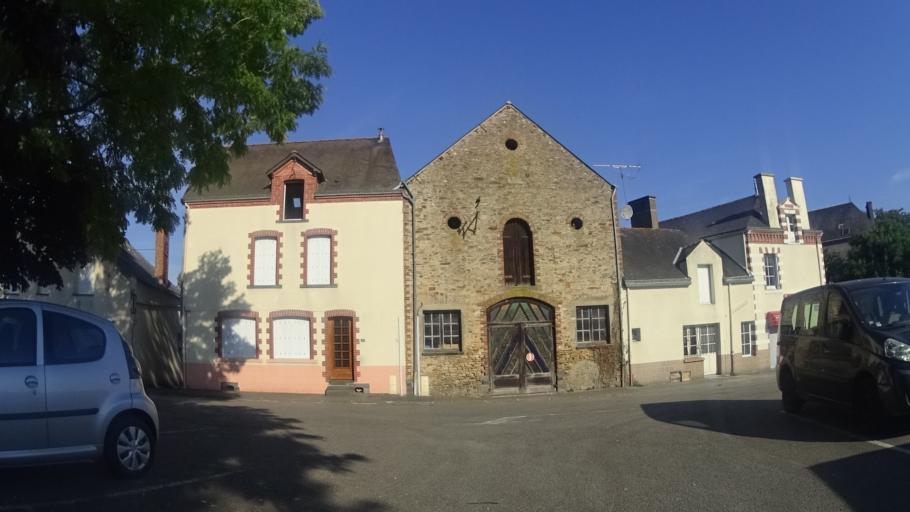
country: FR
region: Pays de la Loire
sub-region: Departement de la Loire-Atlantique
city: Joue-sur-Erdre
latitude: 47.4956
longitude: -1.4200
